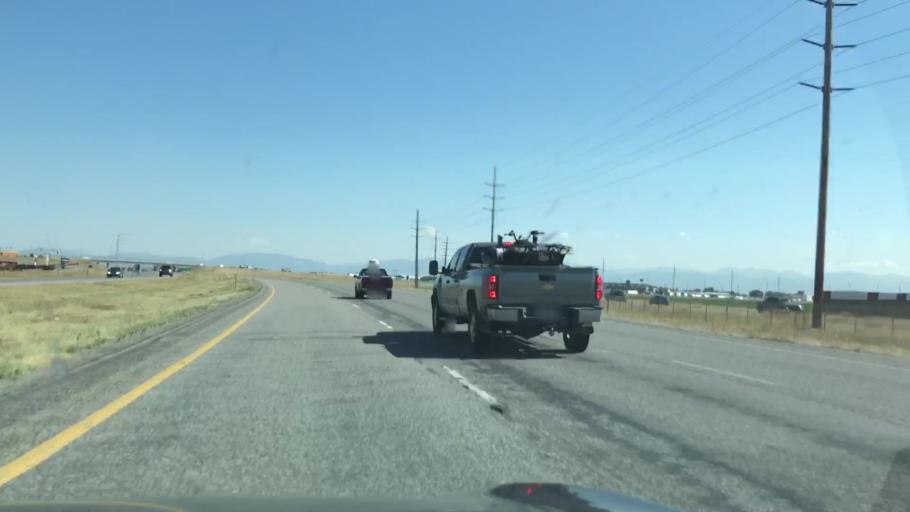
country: US
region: Montana
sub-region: Gallatin County
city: Belgrade
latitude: 45.7713
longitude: -111.1937
